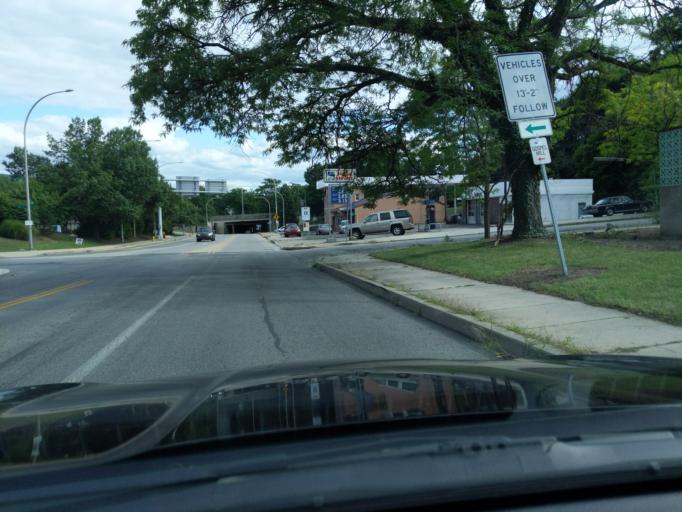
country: US
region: Pennsylvania
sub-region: Blair County
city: Altoona
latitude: 40.5128
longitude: -78.4088
